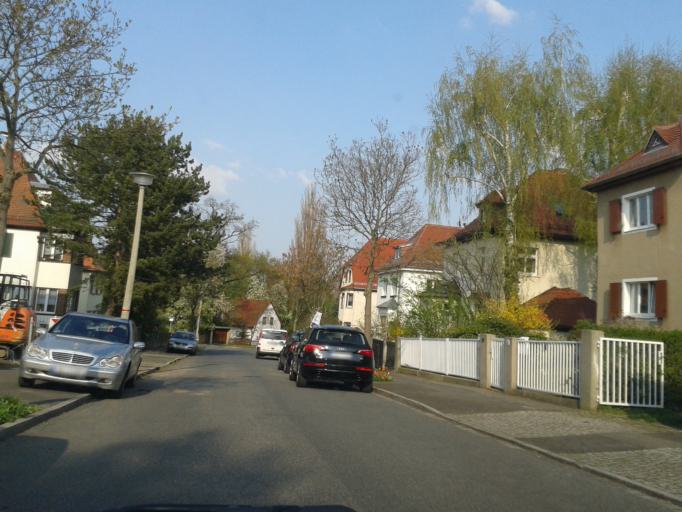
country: DE
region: Saxony
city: Dresden
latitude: 51.0206
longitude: 13.7562
